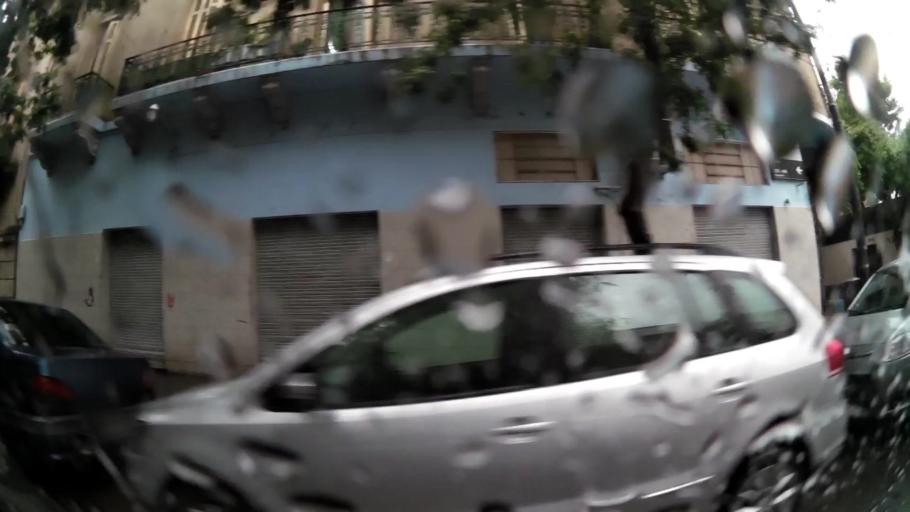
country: AR
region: Buenos Aires
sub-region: Partido de Avellaneda
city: Avellaneda
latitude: -34.6347
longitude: -58.3628
